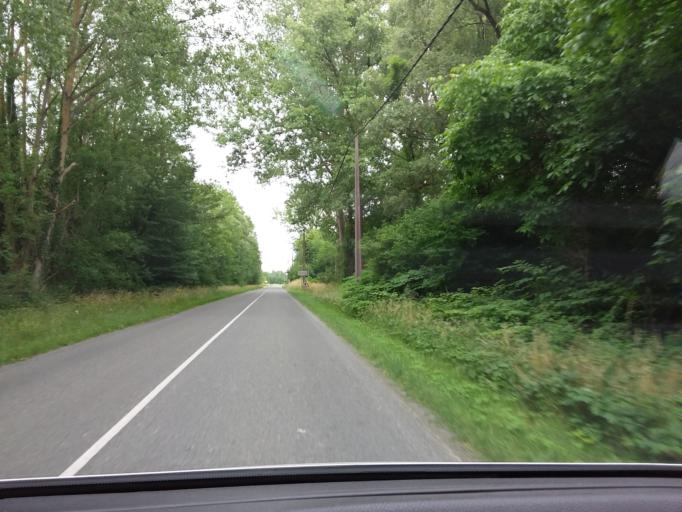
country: FR
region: Champagne-Ardenne
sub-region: Departement de la Marne
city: Fismes
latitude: 49.4003
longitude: 3.6287
